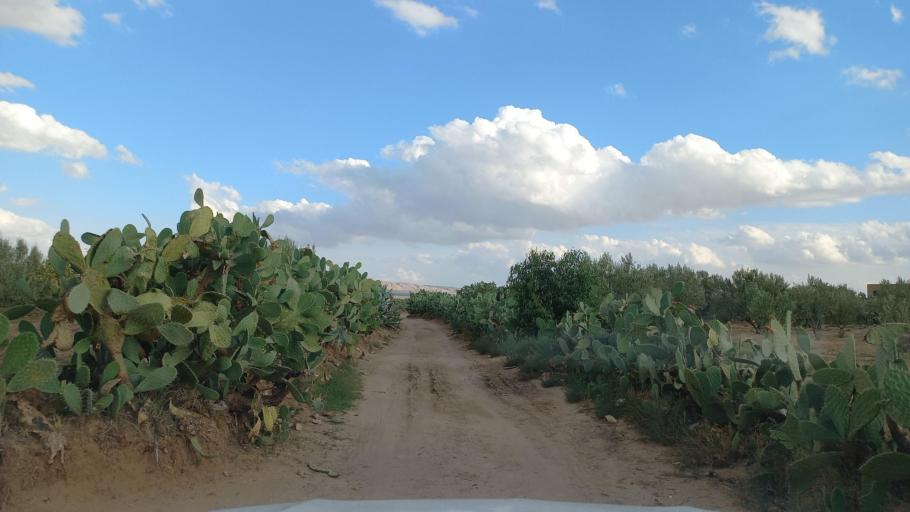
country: TN
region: Al Qasrayn
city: Sbiba
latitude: 35.3849
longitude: 9.0534
